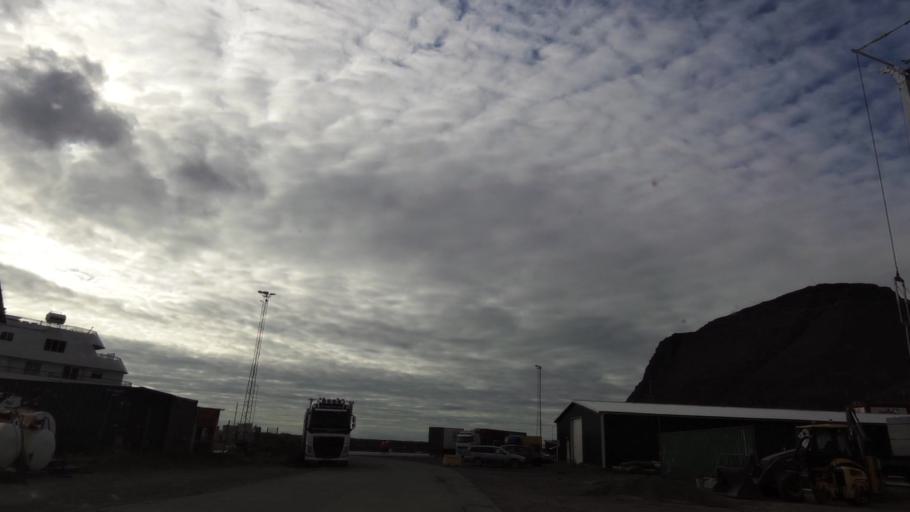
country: IS
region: West
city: Olafsvik
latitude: 65.5958
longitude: -24.0042
